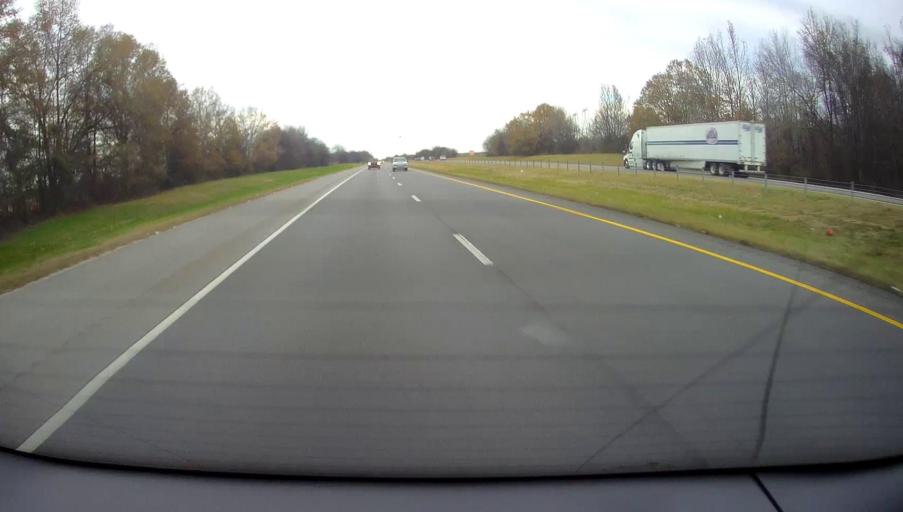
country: US
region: Alabama
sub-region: Morgan County
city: Decatur
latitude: 34.6915
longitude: -86.9262
